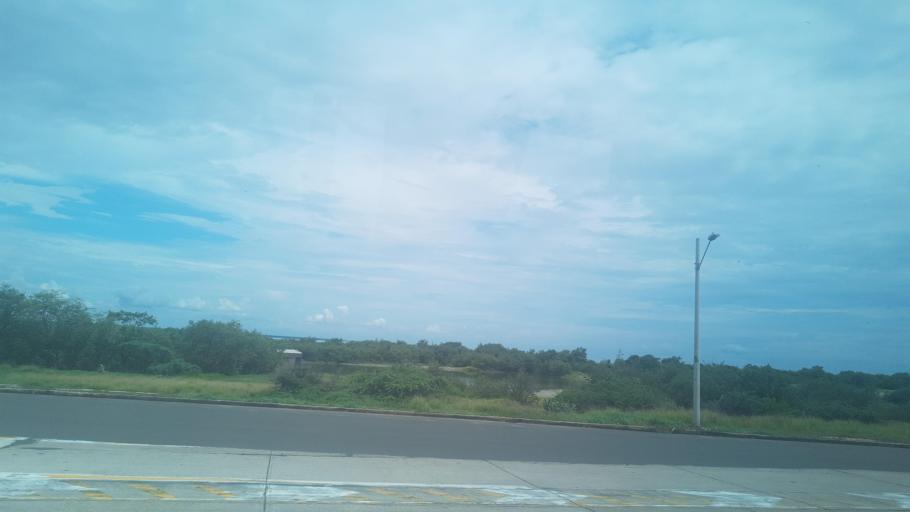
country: CO
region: Magdalena
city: Puebloviejo
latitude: 10.9772
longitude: -74.3371
